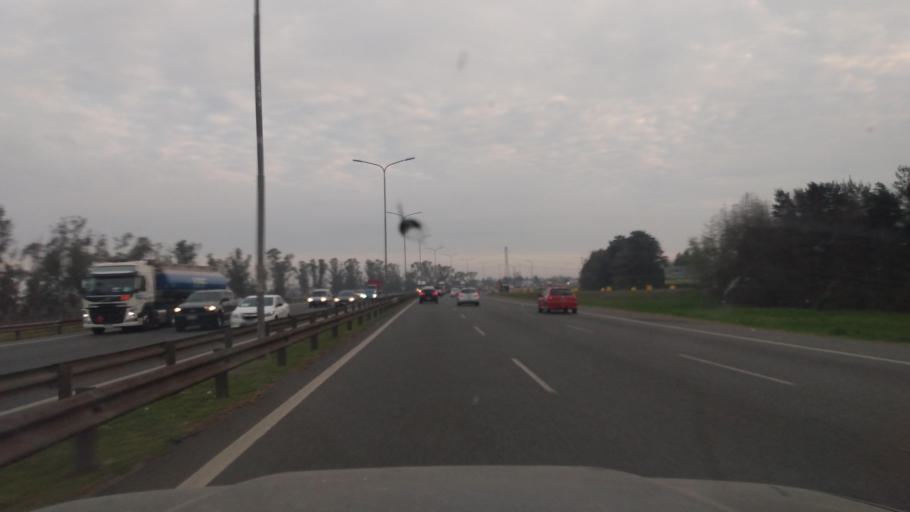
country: AR
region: Buenos Aires
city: Hurlingham
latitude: -34.5456
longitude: -58.6035
